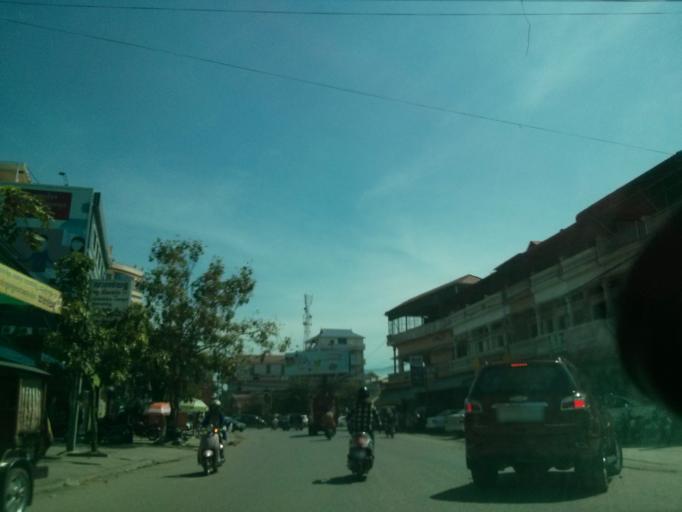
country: KH
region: Phnom Penh
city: Phnom Penh
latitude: 11.5838
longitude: 104.8995
